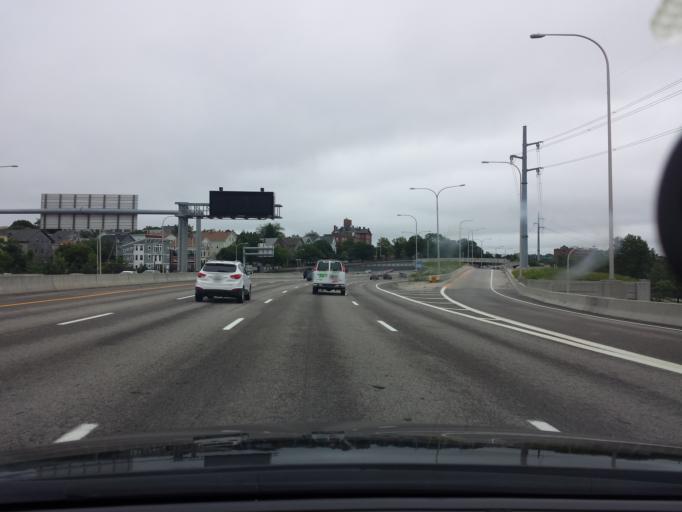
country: US
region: Rhode Island
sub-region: Providence County
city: Providence
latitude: 41.8174
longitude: -71.3981
